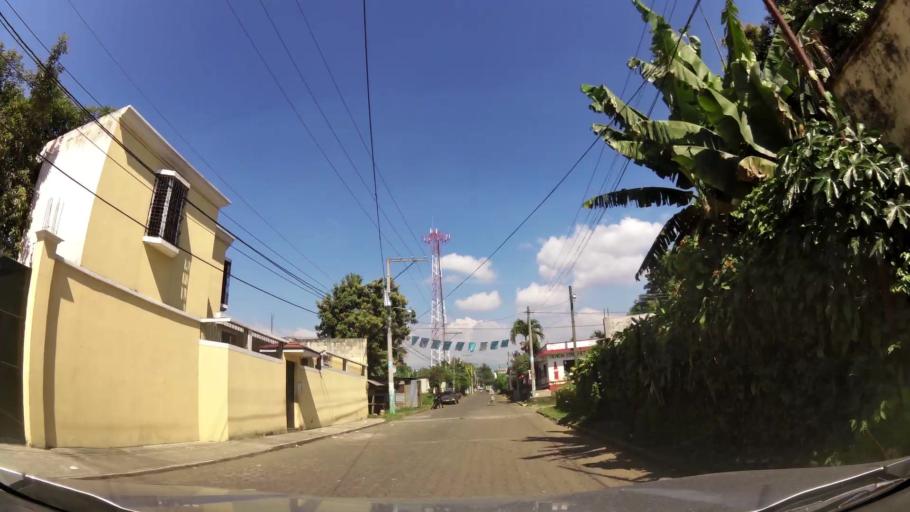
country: GT
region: Suchitepeque
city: Mazatenango
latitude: 14.5315
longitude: -91.4894
